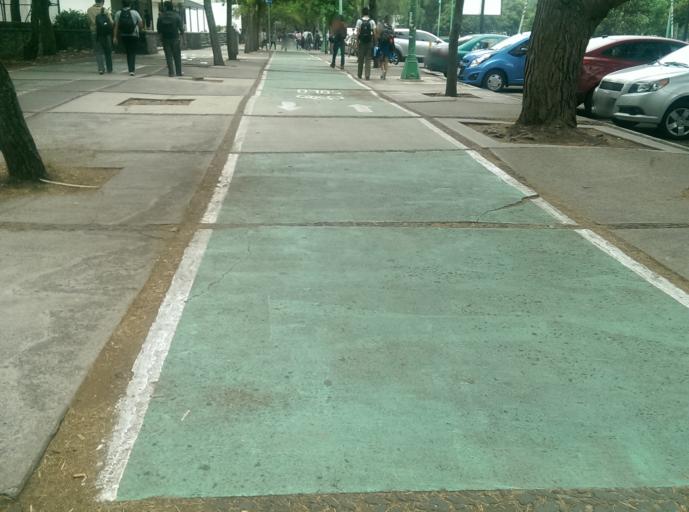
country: MX
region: Mexico City
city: Magdalena Contreras
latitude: 19.3288
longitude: -99.1835
